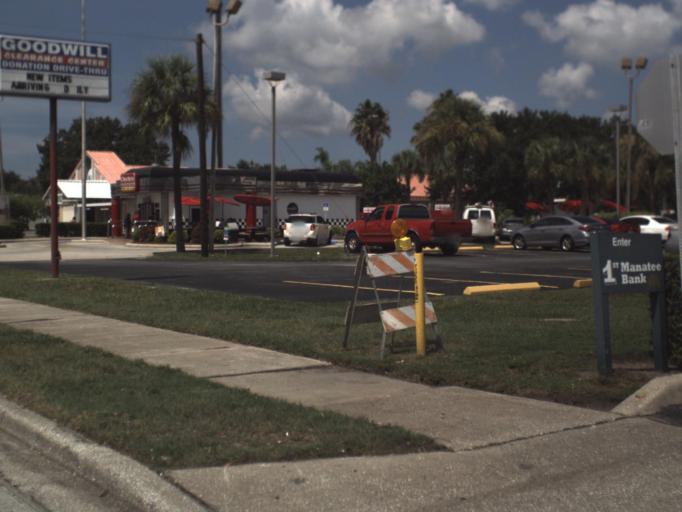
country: US
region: Florida
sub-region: Manatee County
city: South Bradenton
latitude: 27.4626
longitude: -82.6128
